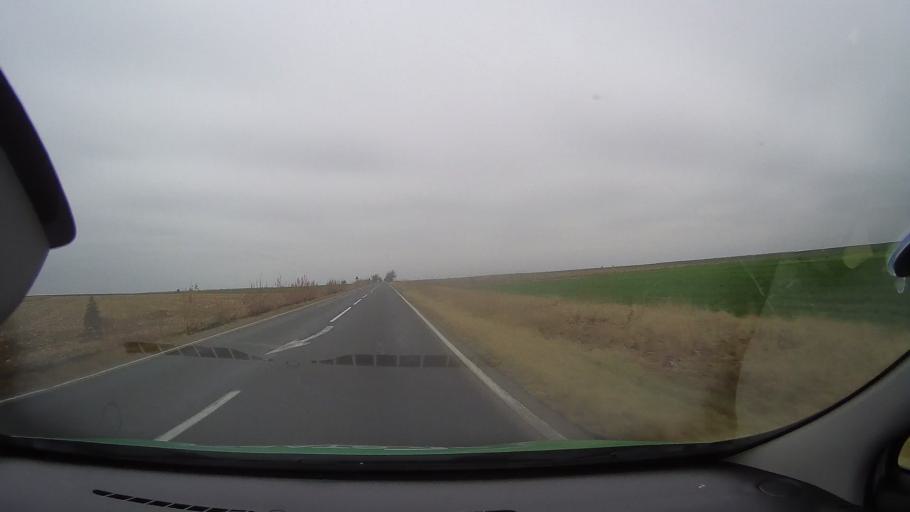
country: RO
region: Braila
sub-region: Comuna Baraganul
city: Baraganul
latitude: 44.7801
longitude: 27.4835
